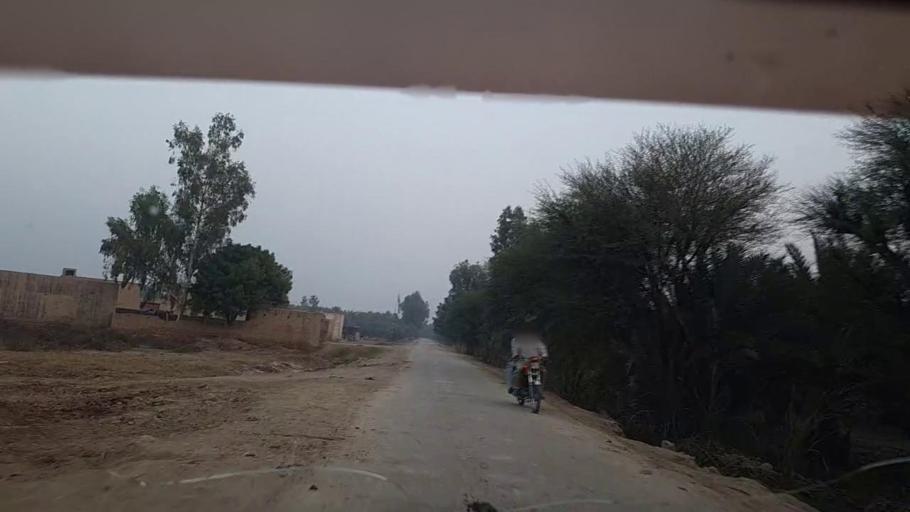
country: PK
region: Sindh
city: Khairpur
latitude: 27.5756
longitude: 68.7220
